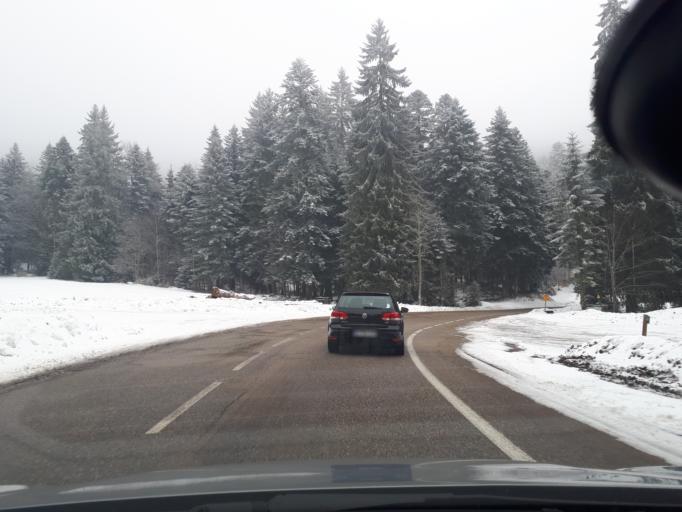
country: FR
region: Rhone-Alpes
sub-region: Departement de l'Isere
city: Vaulnaveys-le-Bas
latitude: 45.1020
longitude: 5.8474
